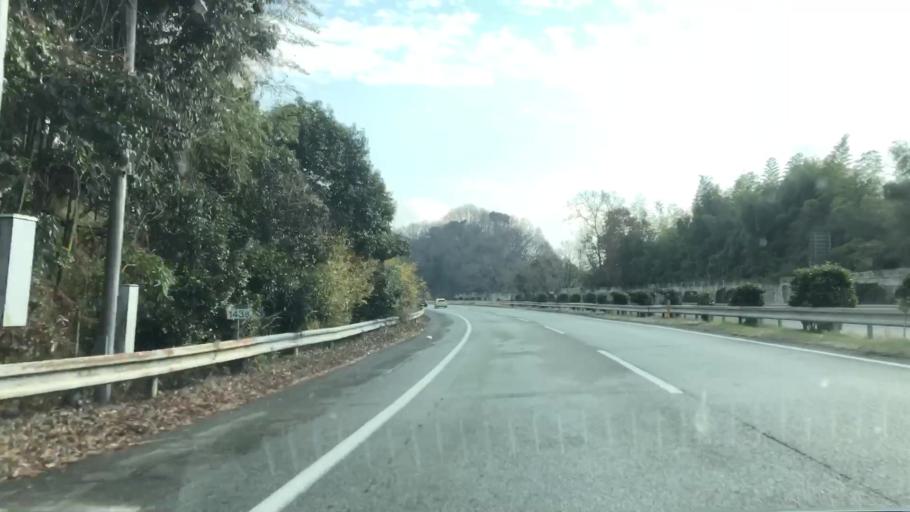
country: JP
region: Kumamoto
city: Tamana
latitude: 33.0051
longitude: 130.5833
